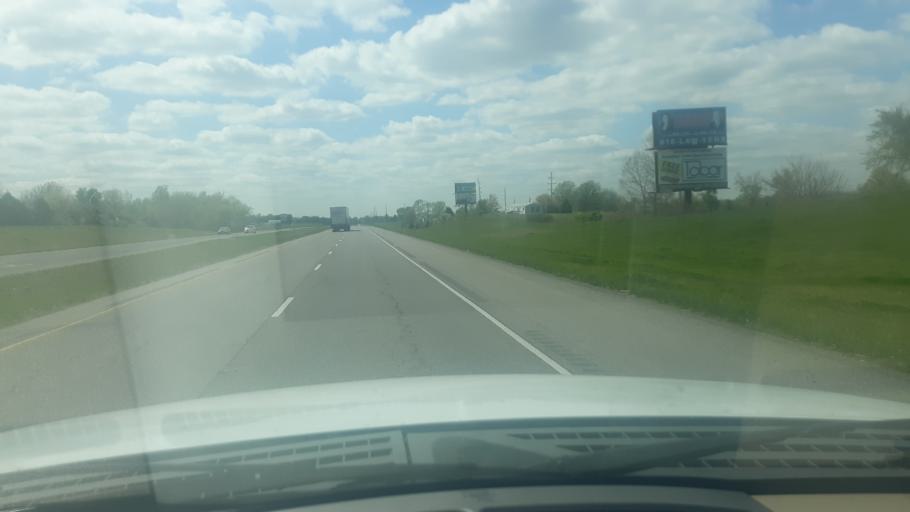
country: US
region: Illinois
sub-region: Williamson County
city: Marion
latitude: 37.7301
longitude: -88.8282
